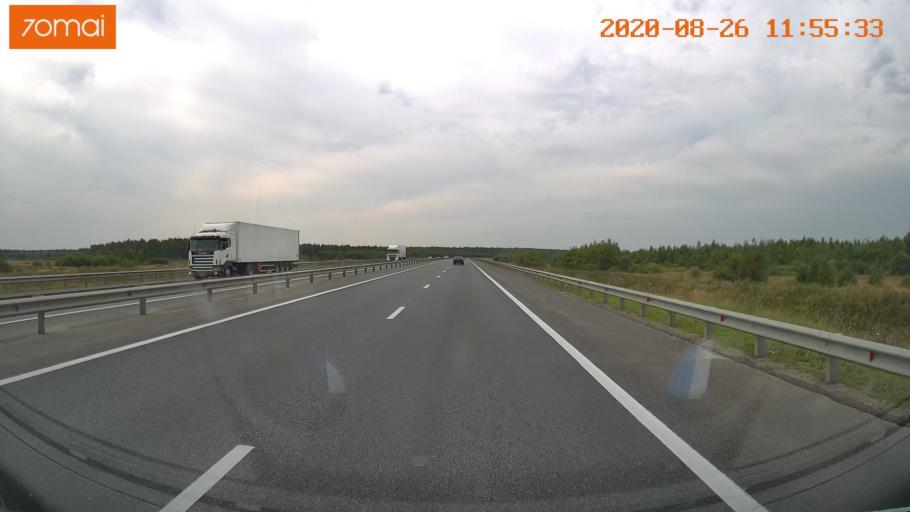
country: RU
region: Rjazan
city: Kiritsy
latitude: 54.2716
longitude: 40.3943
